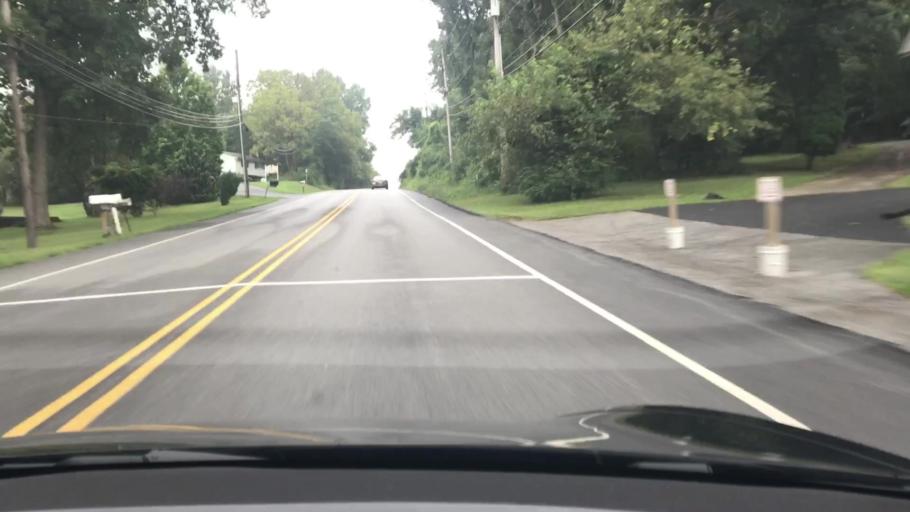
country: US
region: Pennsylvania
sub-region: York County
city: Valley Green
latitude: 40.1682
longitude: -76.8239
